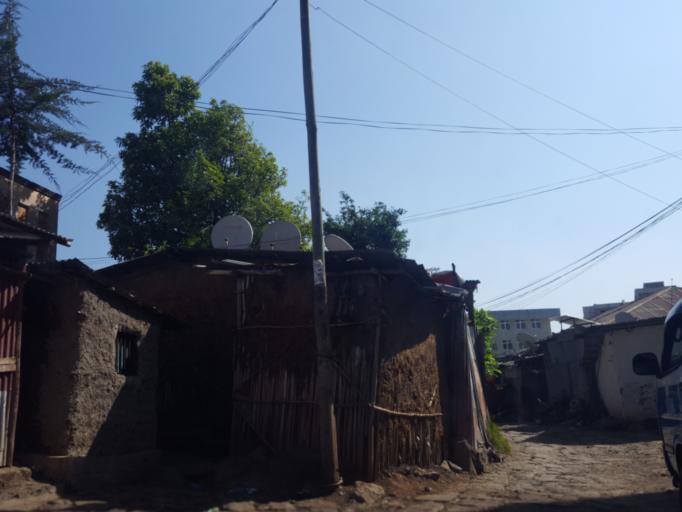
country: ET
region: Adis Abeba
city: Addis Ababa
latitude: 9.0494
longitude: 38.7632
